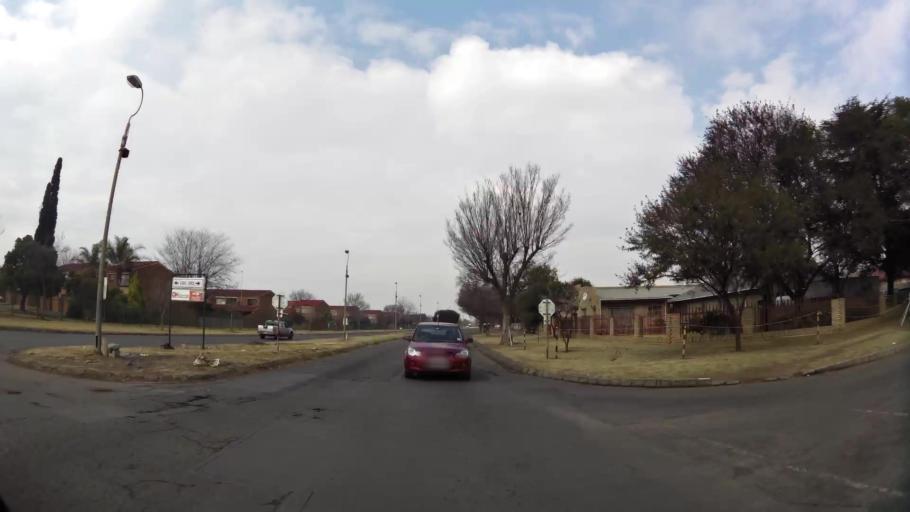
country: ZA
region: Gauteng
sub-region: Sedibeng District Municipality
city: Vanderbijlpark
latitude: -26.6923
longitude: 27.8472
